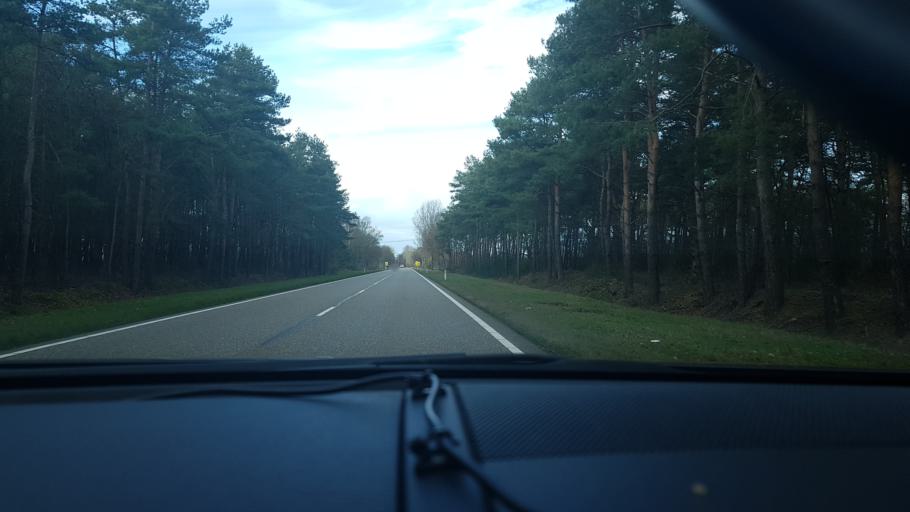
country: NL
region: Limburg
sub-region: Gemeente Peel en Maas
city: Maasbree
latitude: 51.3244
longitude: 6.0430
